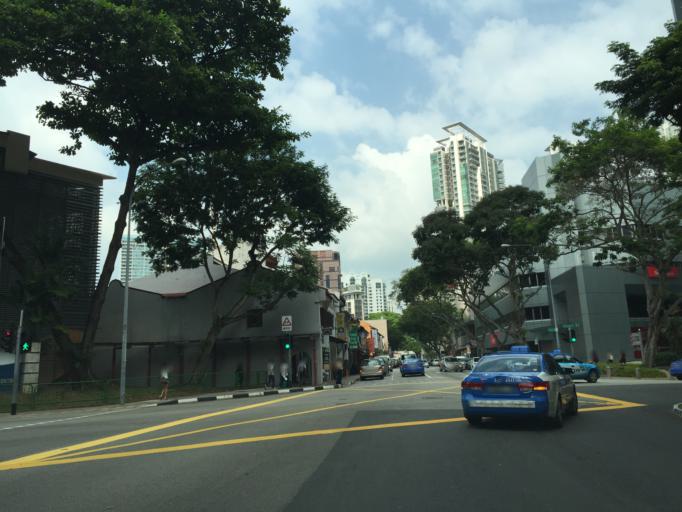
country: SG
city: Singapore
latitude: 1.2994
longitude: 103.8398
